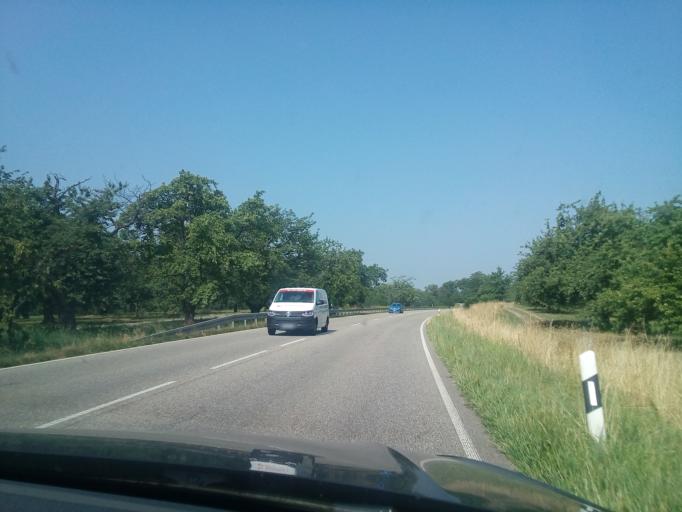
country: DE
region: Baden-Wuerttemberg
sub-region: Freiburg Region
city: Achern
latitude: 48.6118
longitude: 8.0721
